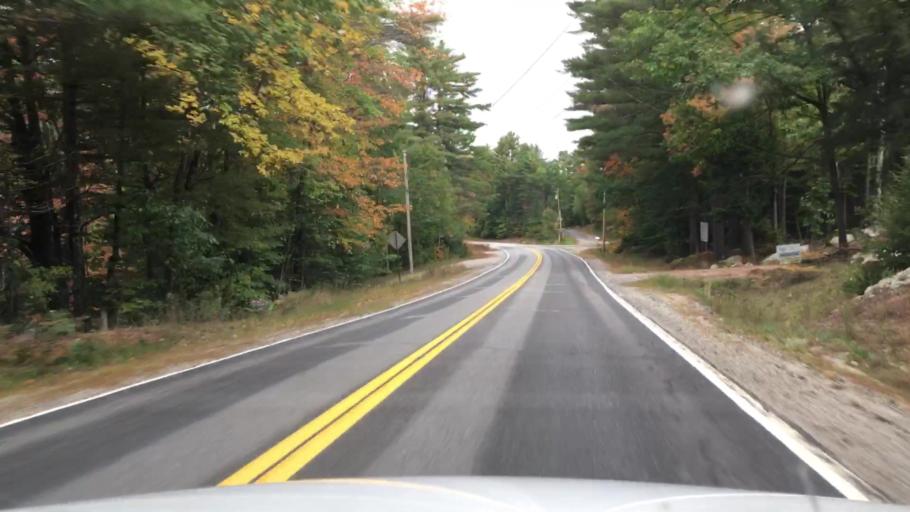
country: US
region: Maine
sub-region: Oxford County
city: Bethel
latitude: 44.3428
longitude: -70.7844
